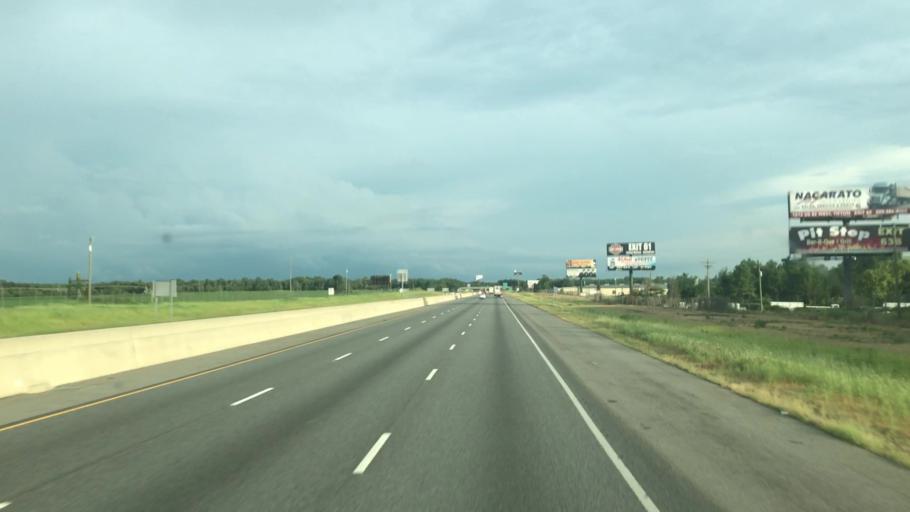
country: US
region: Georgia
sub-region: Turner County
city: Ashburn
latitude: 31.7043
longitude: -83.6340
